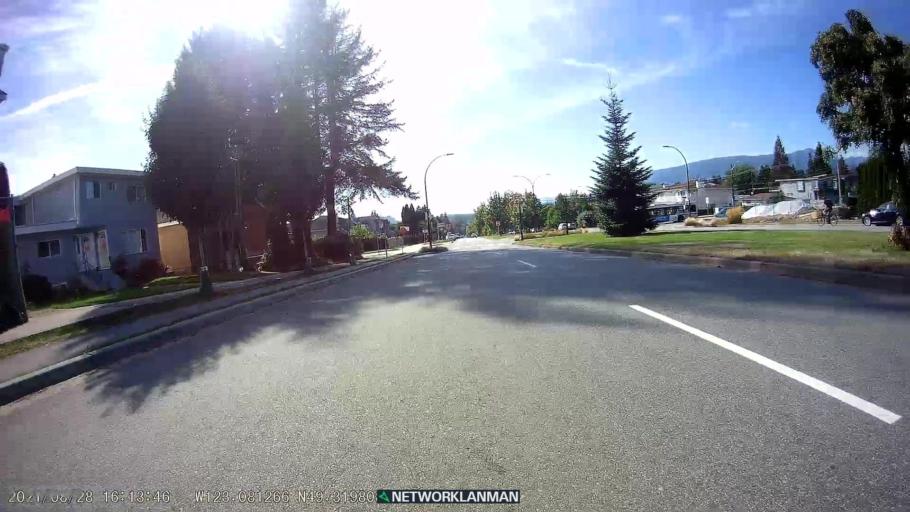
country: CA
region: British Columbia
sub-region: Fraser Valley Regional District
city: North Vancouver
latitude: 49.3190
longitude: -123.0812
